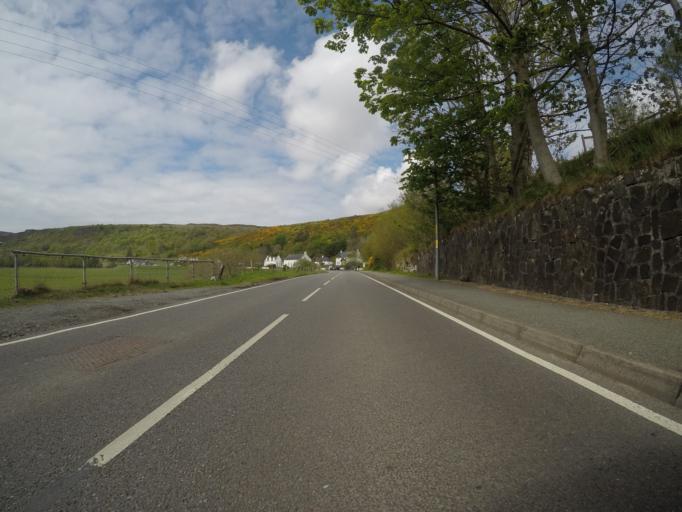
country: GB
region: Scotland
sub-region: Highland
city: Portree
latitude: 57.5902
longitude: -6.3552
